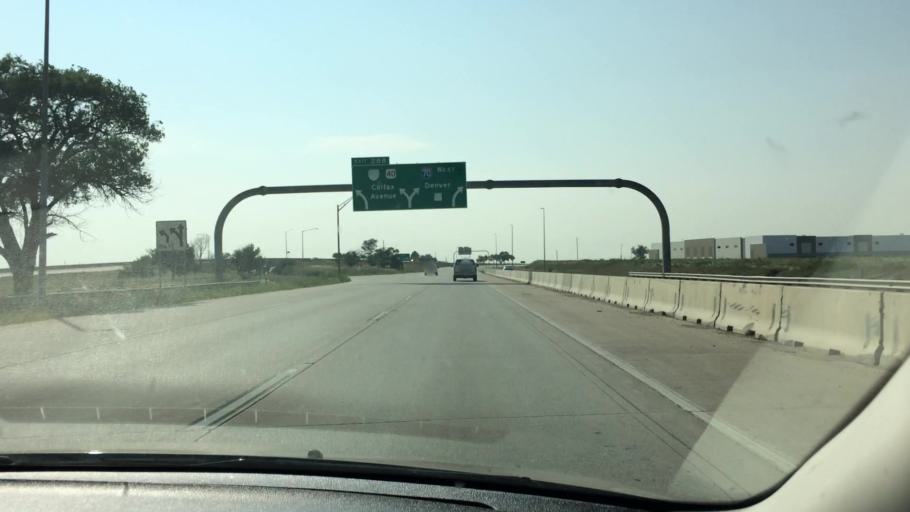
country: US
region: Colorado
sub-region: Adams County
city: Aurora
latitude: 39.7407
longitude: -104.7294
